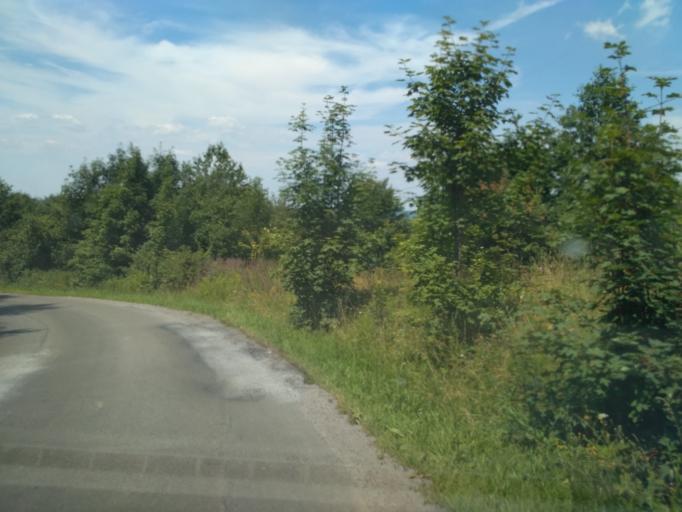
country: PL
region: Subcarpathian Voivodeship
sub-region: Powiat strzyzowski
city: Jawornik
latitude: 49.8727
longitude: 21.8581
